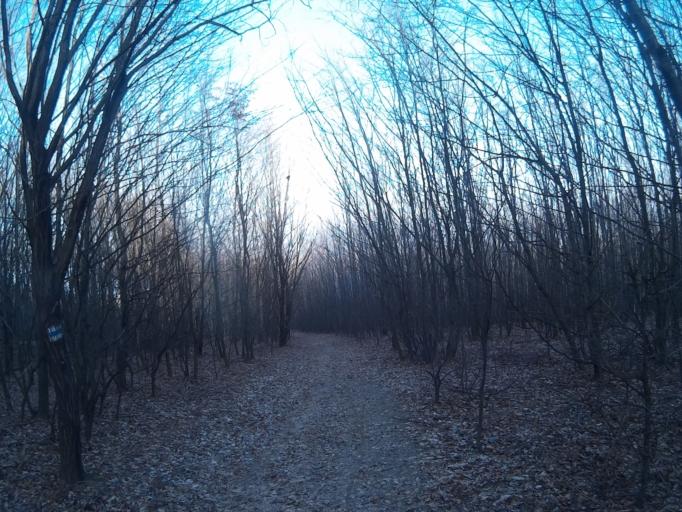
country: HU
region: Nograd
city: Bercel
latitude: 47.9139
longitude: 19.4164
